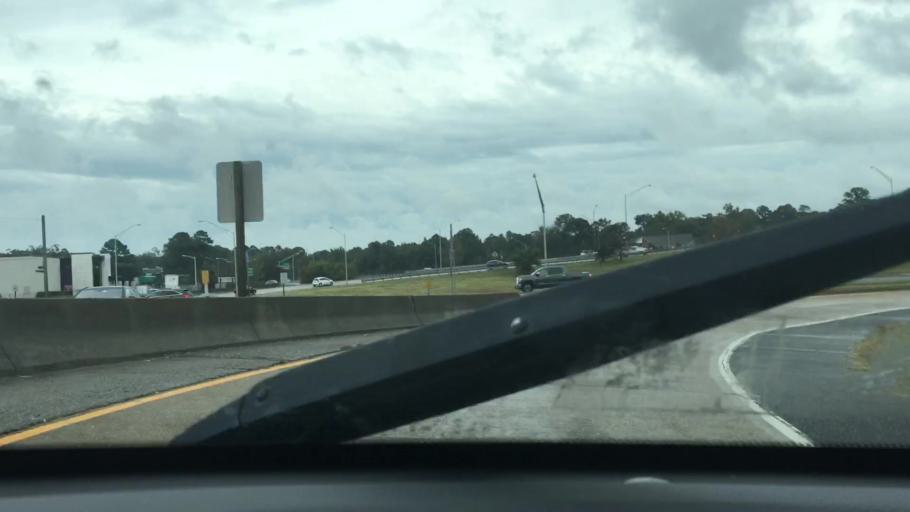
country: US
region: Virginia
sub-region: City of Virginia Beach
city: Virginia Beach
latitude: 36.8371
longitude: -76.0661
